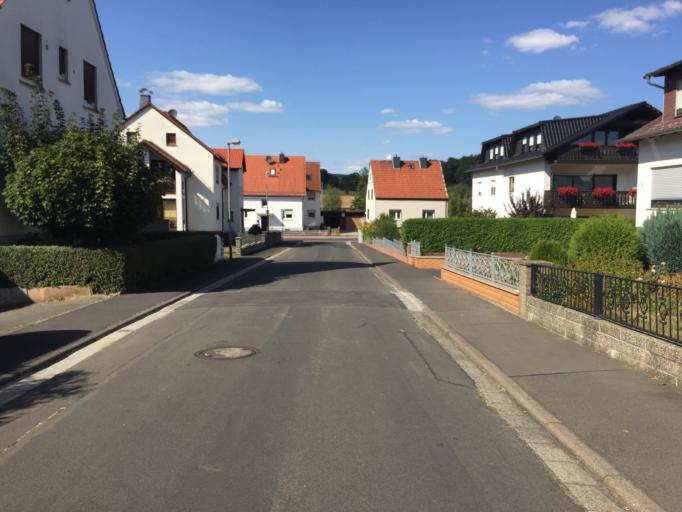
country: DE
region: Hesse
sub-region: Regierungsbezirk Giessen
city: Grunberg
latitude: 50.5971
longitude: 8.9262
